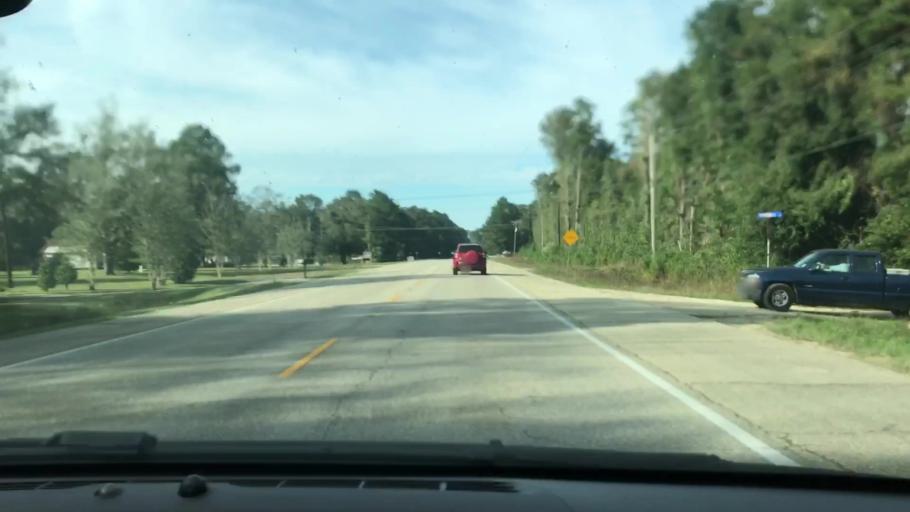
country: US
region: Mississippi
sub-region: Pearl River County
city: Nicholson
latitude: 30.4931
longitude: -89.8118
